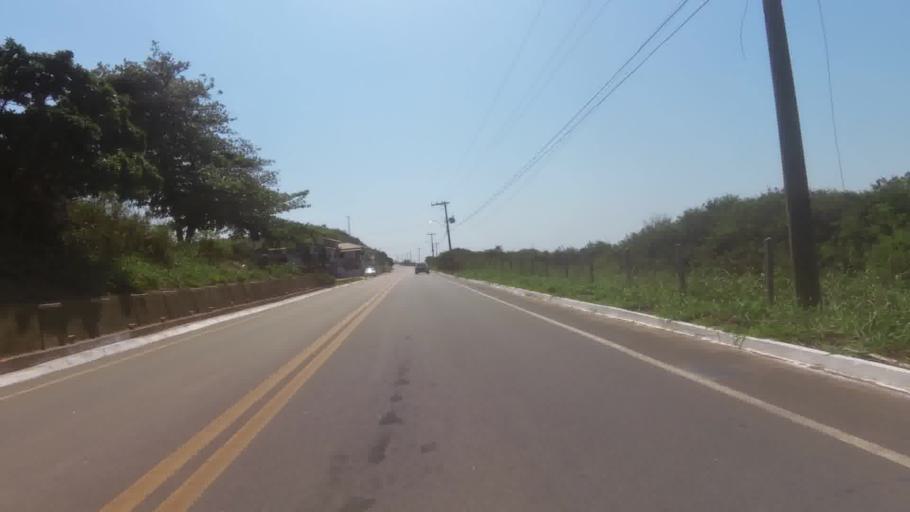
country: BR
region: Espirito Santo
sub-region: Marataizes
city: Marataizes
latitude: -21.0980
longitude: -40.8486
